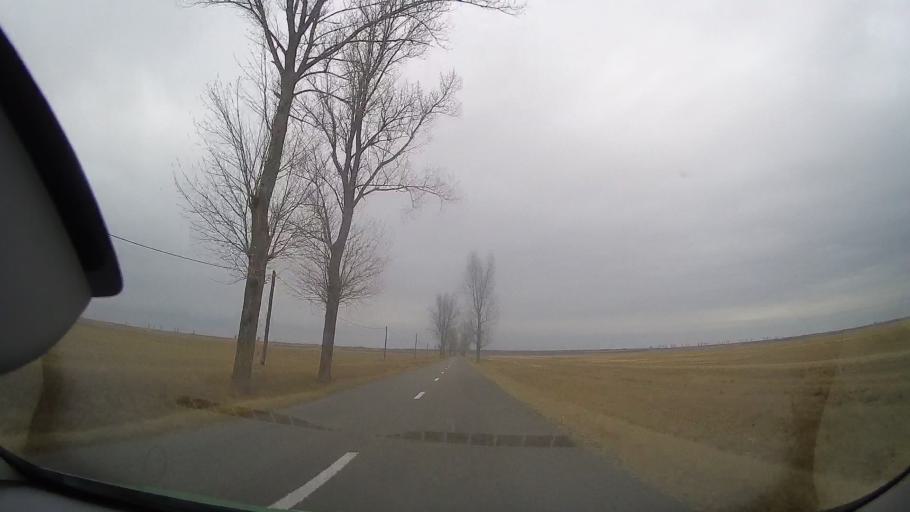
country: RO
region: Braila
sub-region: Comuna Rosiori
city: Rosiori
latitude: 44.8232
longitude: 27.4006
